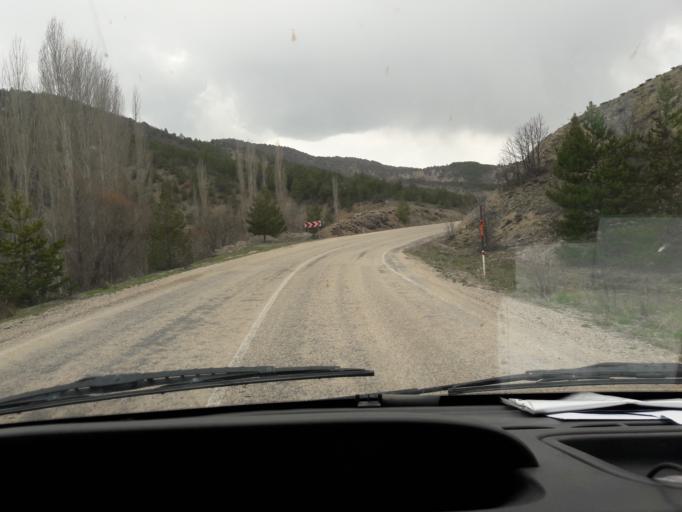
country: TR
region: Giresun
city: Alucra
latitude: 40.2748
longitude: 38.8294
